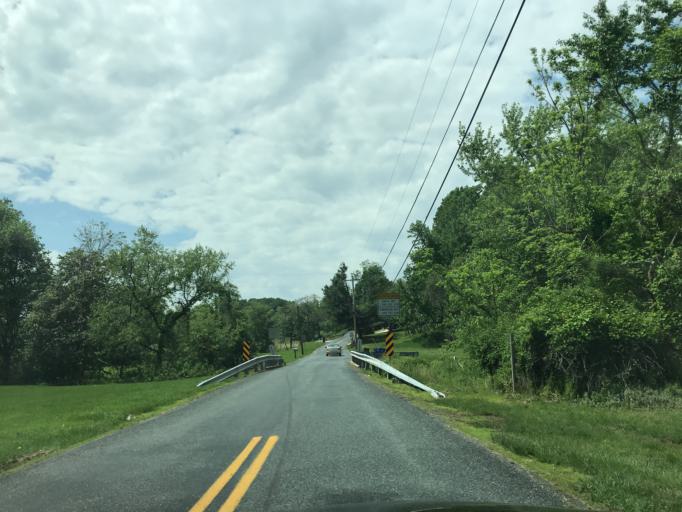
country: US
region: Maryland
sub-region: Harford County
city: Bel Air North
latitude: 39.6056
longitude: -76.3488
